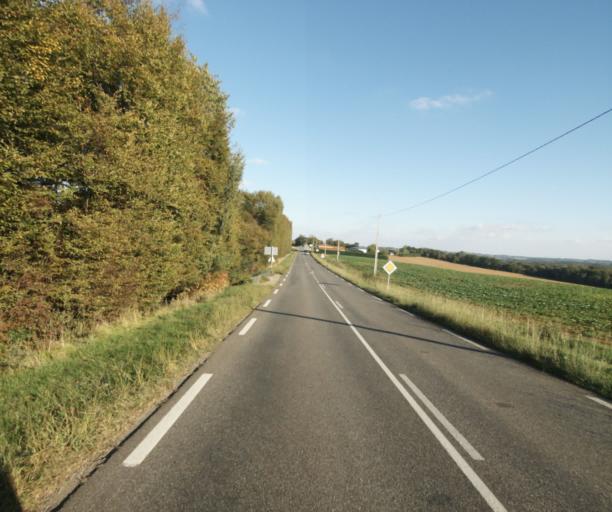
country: FR
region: Midi-Pyrenees
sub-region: Departement du Gers
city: Eauze
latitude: 43.7703
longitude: 0.1316
